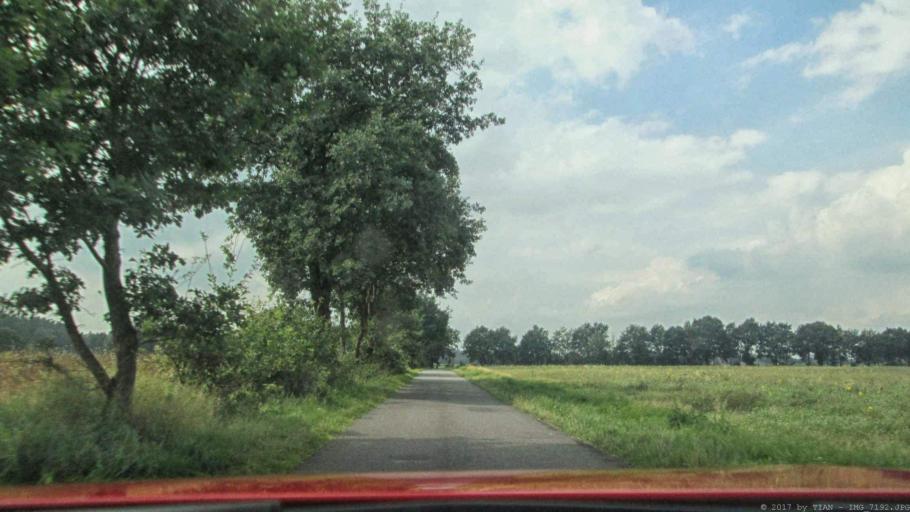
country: DE
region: Lower Saxony
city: Neetze
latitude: 53.2953
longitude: 10.6352
